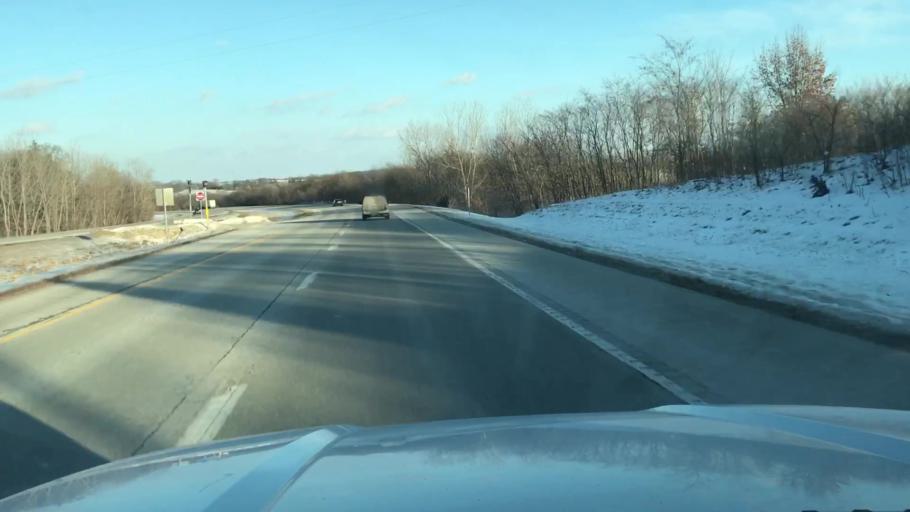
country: US
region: Missouri
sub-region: Clinton County
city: Gower
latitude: 39.7469
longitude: -94.6095
